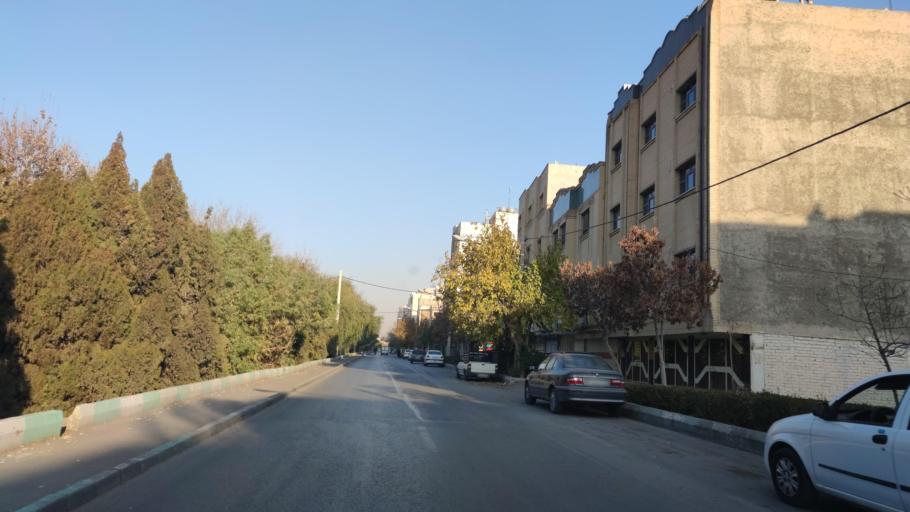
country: IR
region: Isfahan
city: Isfahan
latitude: 32.7083
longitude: 51.6831
